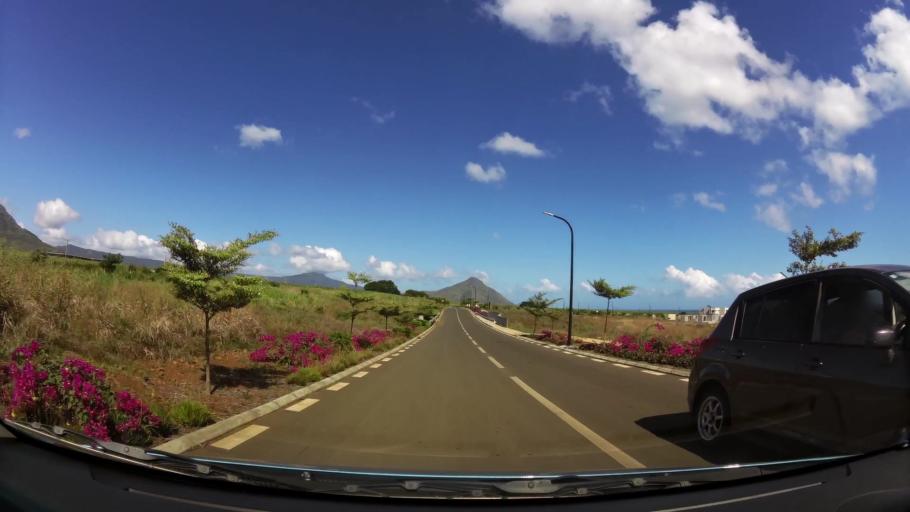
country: MU
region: Black River
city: Cascavelle
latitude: -20.2801
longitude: 57.3920
